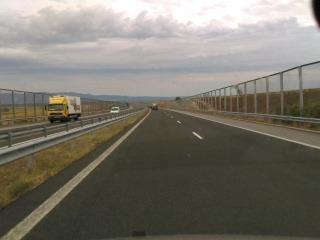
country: BG
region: Yambol
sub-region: Obshtina Yambol
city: Yambol
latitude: 42.5186
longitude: 26.3783
